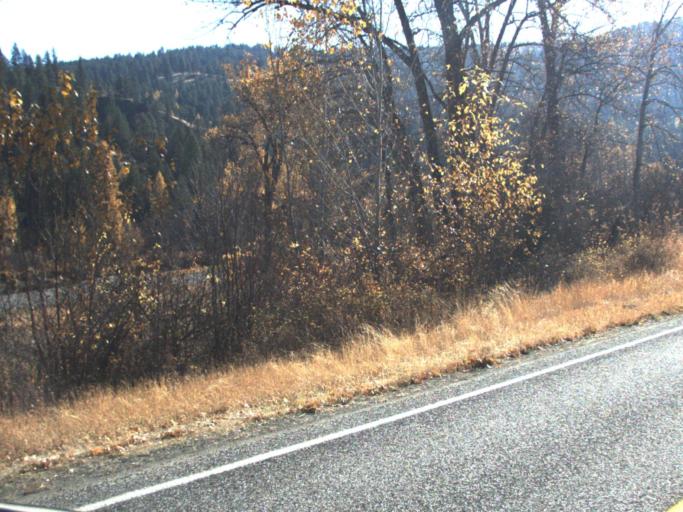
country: CA
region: British Columbia
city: Grand Forks
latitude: 48.9244
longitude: -118.5665
